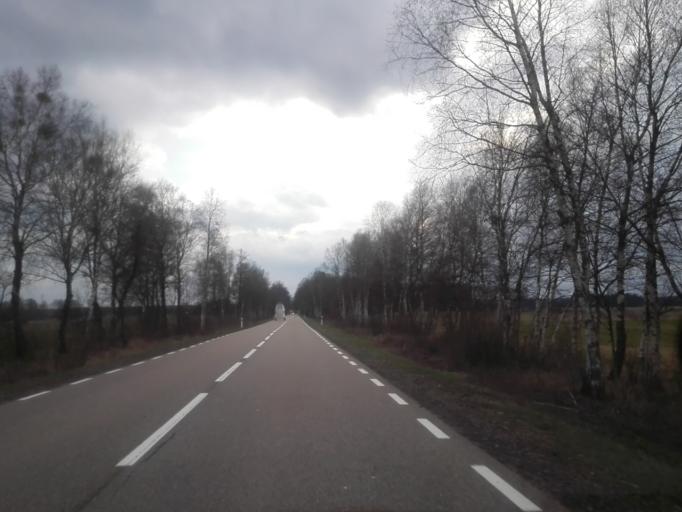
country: PL
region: Podlasie
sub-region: Powiat sejnenski
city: Krasnopol
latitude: 53.9479
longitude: 23.1958
